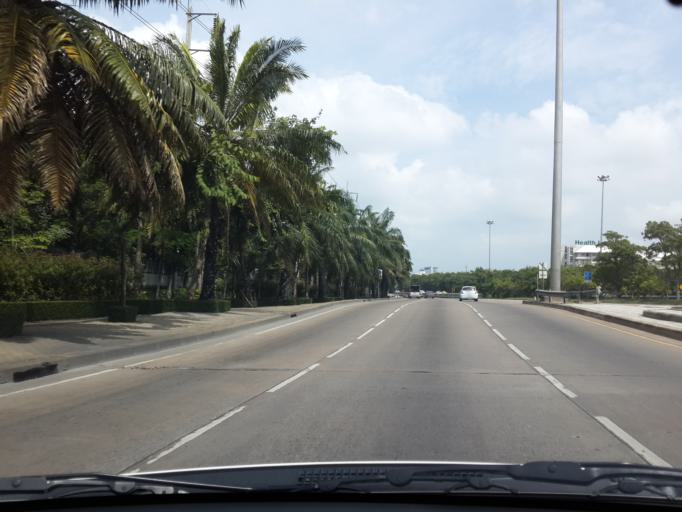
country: TH
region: Bangkok
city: Wang Thonglang
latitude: 13.7717
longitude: 100.6055
